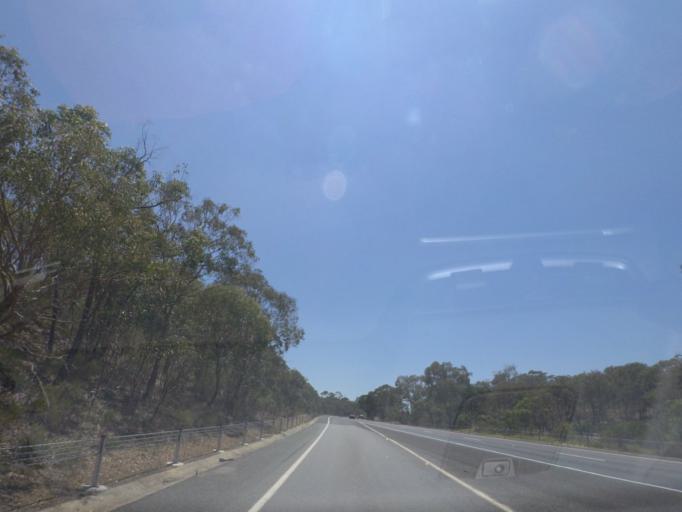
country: AU
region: Victoria
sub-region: Murrindindi
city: Kinglake West
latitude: -36.9617
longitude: 145.1834
